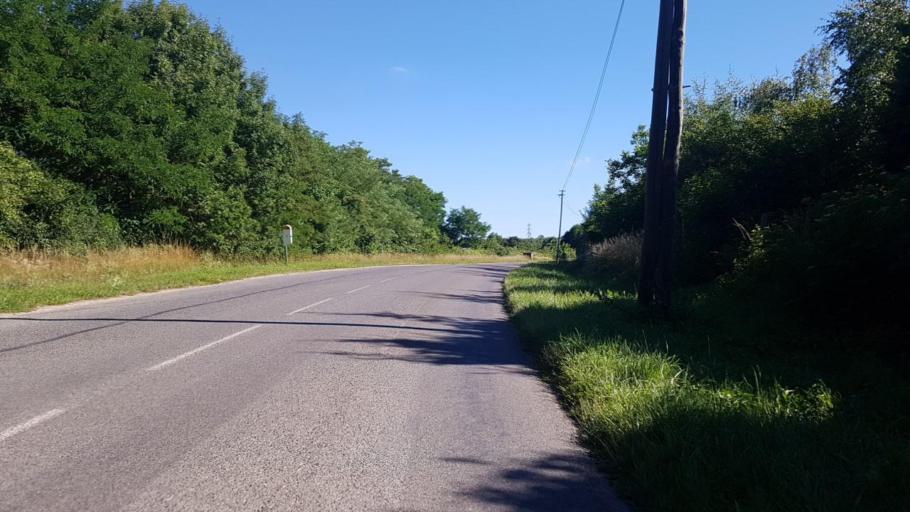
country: FR
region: Ile-de-France
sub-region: Departement de Seine-et-Marne
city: Esbly
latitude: 48.9381
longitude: 2.7994
